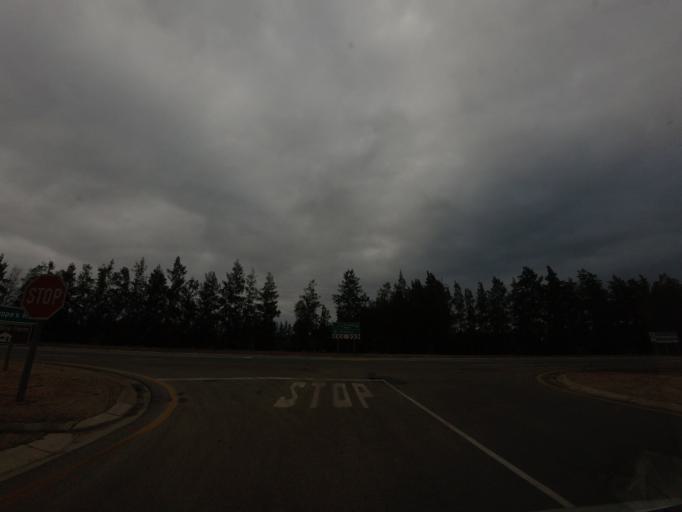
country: ZA
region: Mpumalanga
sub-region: Ehlanzeni District
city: Komatipoort
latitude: -25.4487
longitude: 31.6695
